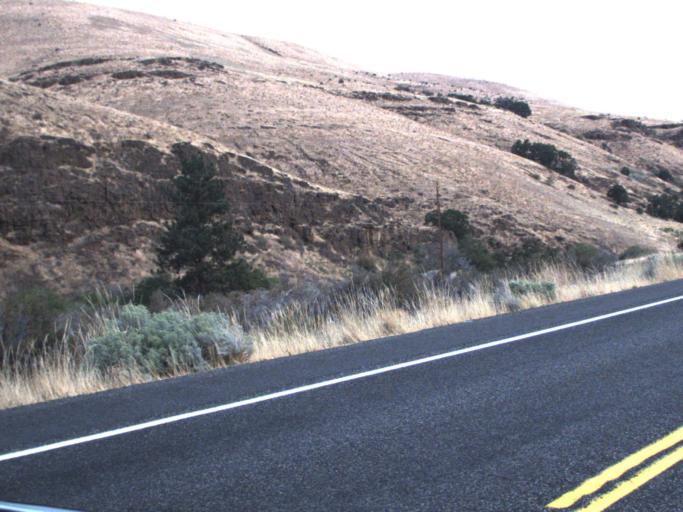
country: US
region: Washington
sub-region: Yakima County
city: Toppenish
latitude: 46.0897
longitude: -120.5507
